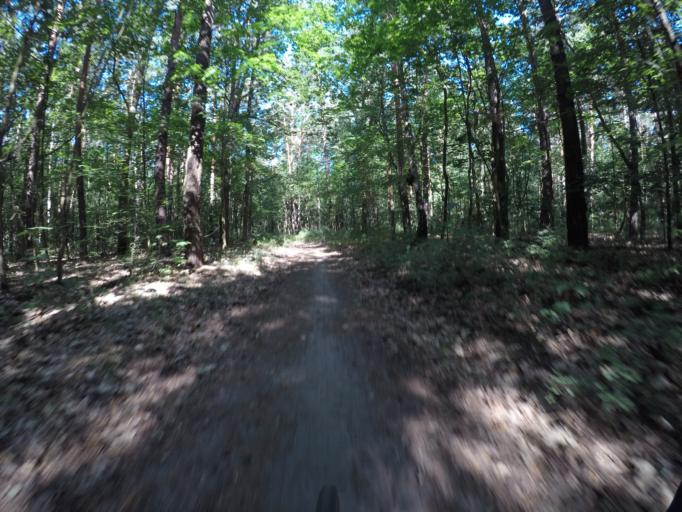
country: DE
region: Berlin
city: Rahnsdorf
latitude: 52.4516
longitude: 13.6990
